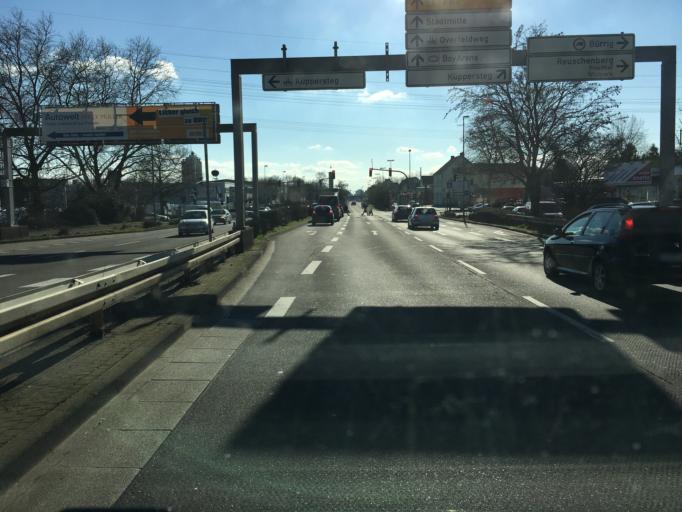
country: DE
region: North Rhine-Westphalia
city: Opladen
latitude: 51.0536
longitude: 6.9996
